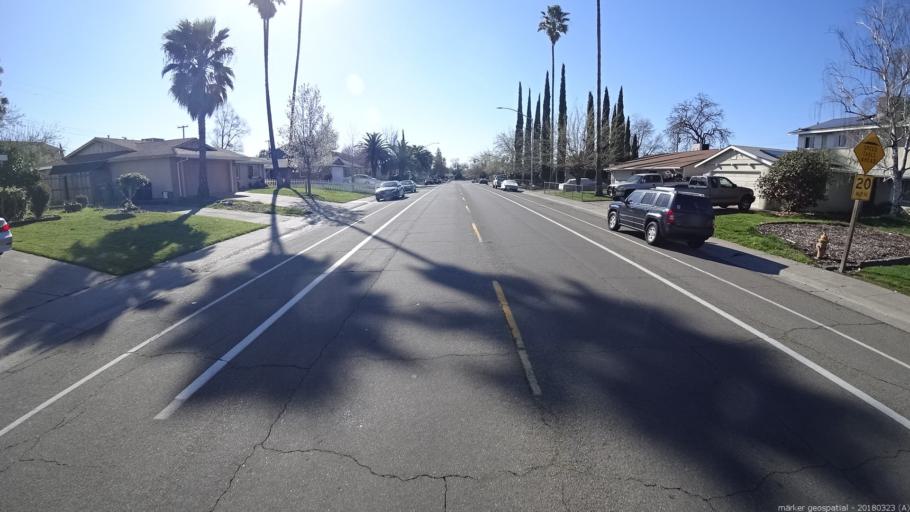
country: US
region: California
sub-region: Sacramento County
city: North Highlands
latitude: 38.7007
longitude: -121.3776
